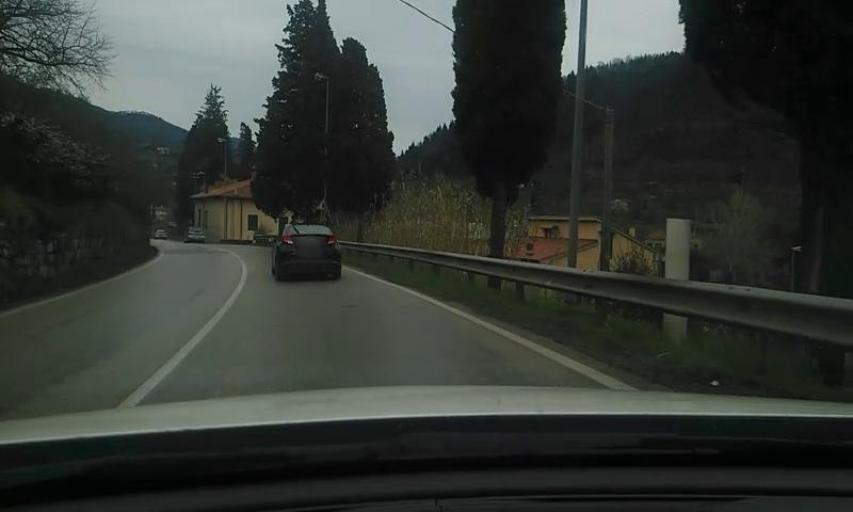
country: IT
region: Tuscany
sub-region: Provincia di Prato
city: Vaiano
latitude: 43.9403
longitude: 11.1281
